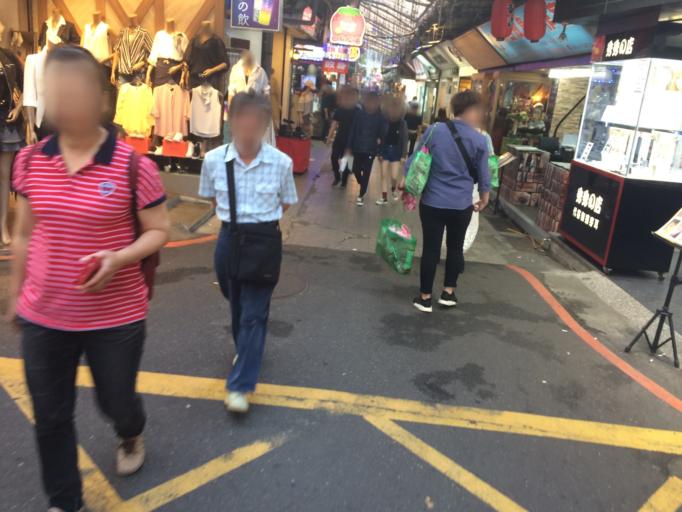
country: TW
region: Taipei
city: Taipei
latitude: 25.0441
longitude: 121.5069
